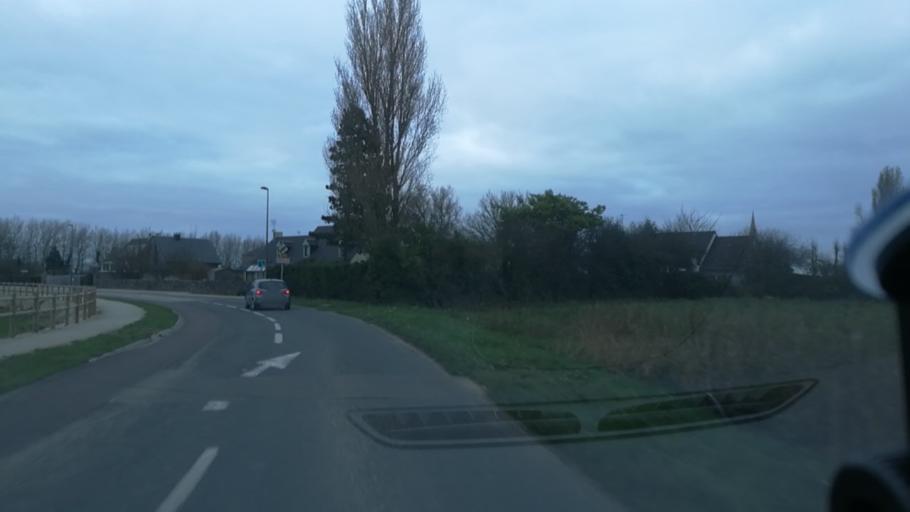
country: FR
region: Lower Normandy
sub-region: Departement de la Manche
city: Reville
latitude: 49.6146
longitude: -1.2587
